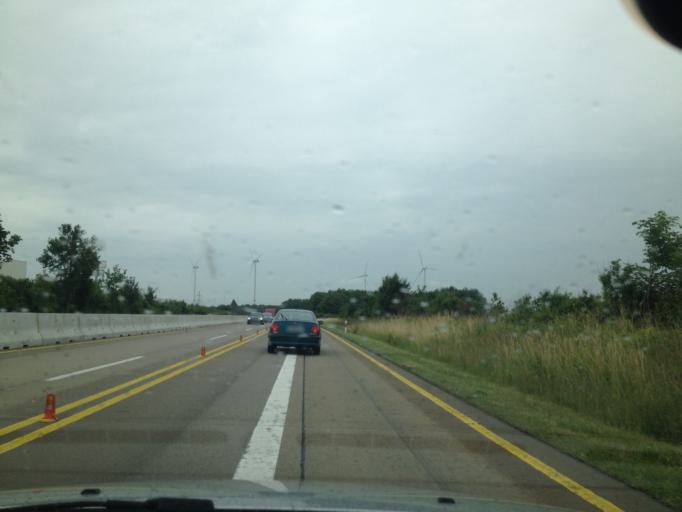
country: DE
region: Bavaria
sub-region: Regierungsbezirk Mittelfranken
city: Uffenheim
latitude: 49.5170
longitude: 10.1966
